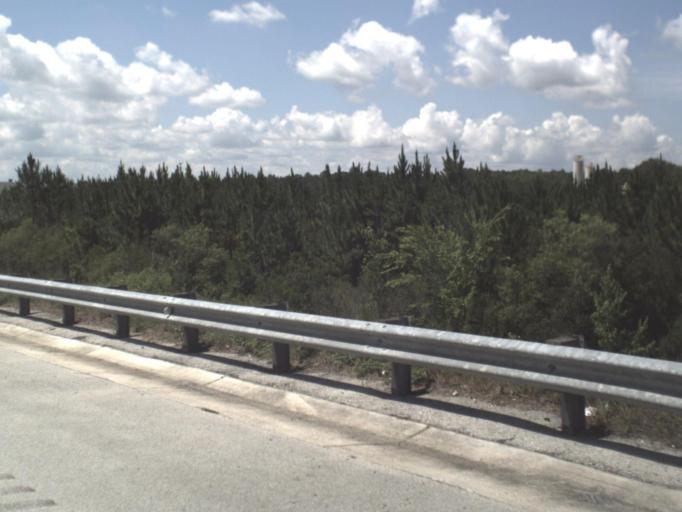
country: US
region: Florida
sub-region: Saint Johns County
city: Saint Augustine South
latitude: 29.8394
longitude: -81.3862
